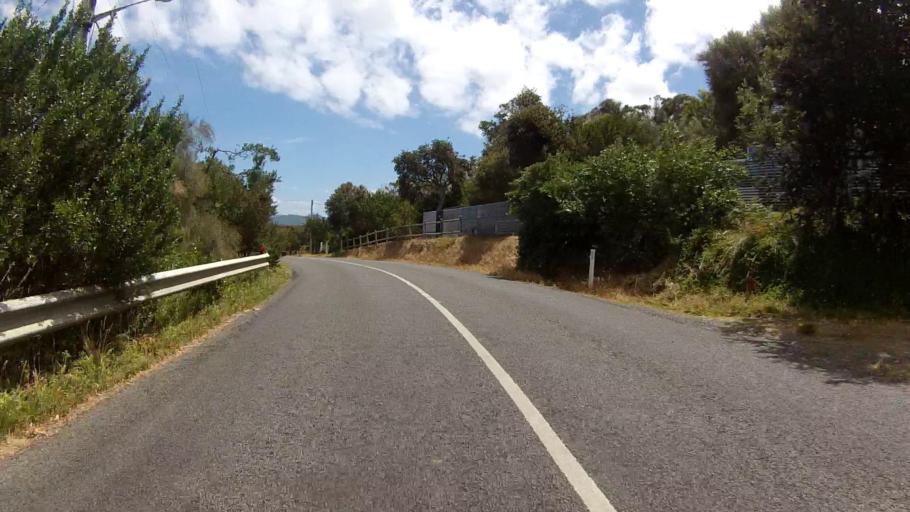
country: AU
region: Tasmania
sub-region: Sorell
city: Sorell
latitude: -42.8667
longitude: 147.6166
